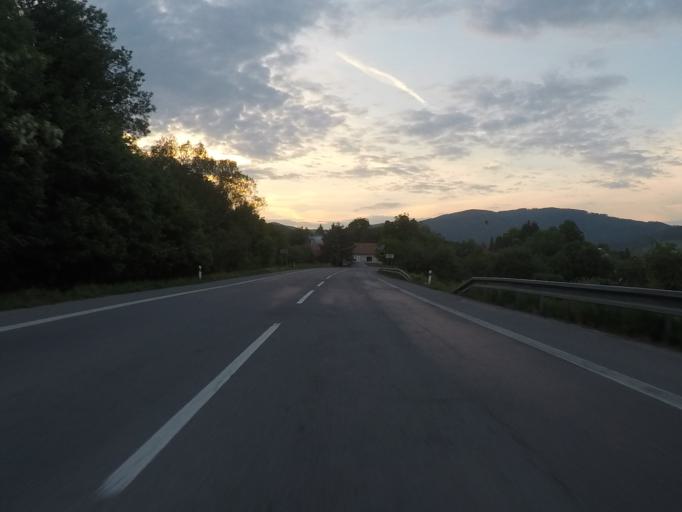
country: SK
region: Banskobystricky
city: Rimavska Sobota
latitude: 48.4984
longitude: 19.9365
